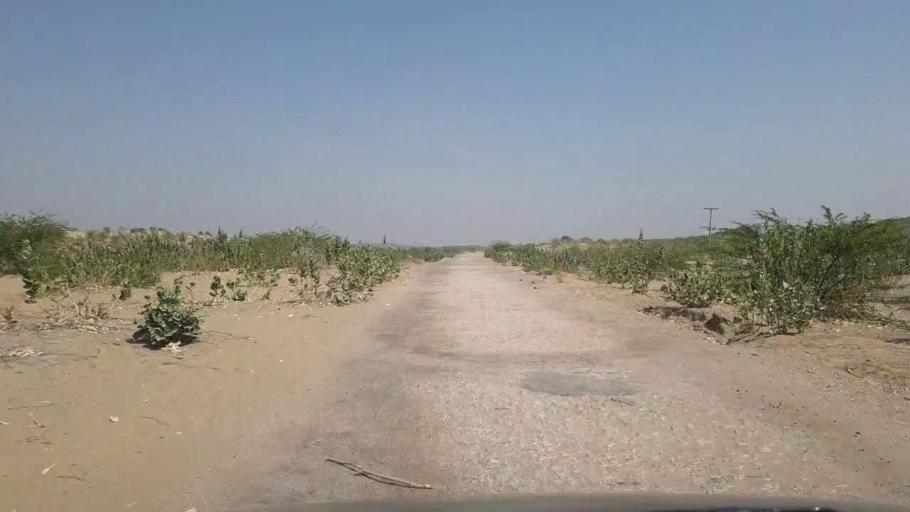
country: PK
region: Sindh
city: Chor
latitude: 25.7018
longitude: 70.2001
